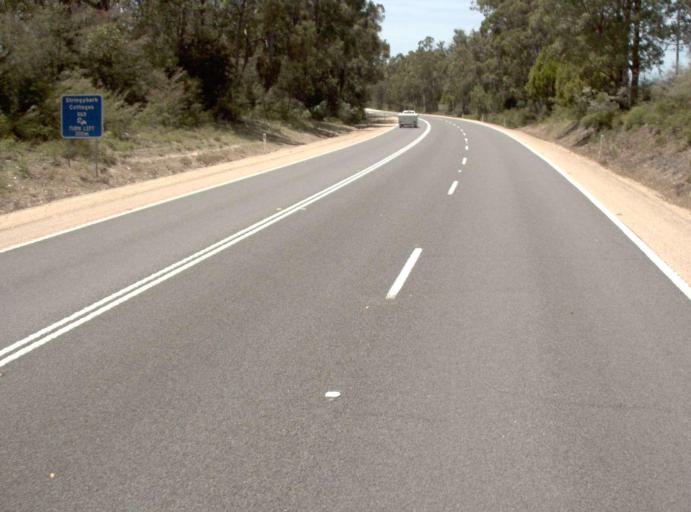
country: AU
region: Victoria
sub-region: East Gippsland
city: Bairnsdale
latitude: -37.7325
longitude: 147.7841
